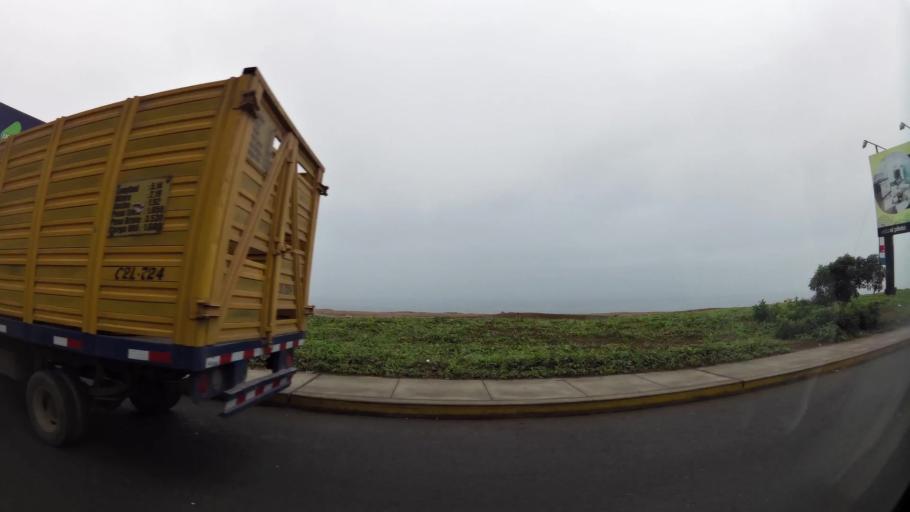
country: PE
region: Callao
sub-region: Callao
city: Callao
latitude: -12.0807
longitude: -77.1076
